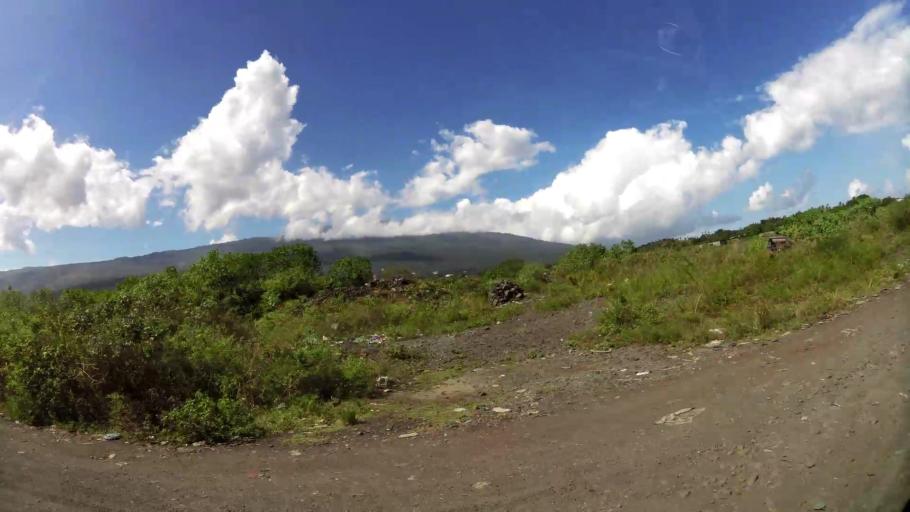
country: KM
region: Grande Comore
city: Mavingouni
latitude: -11.7254
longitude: 43.2384
